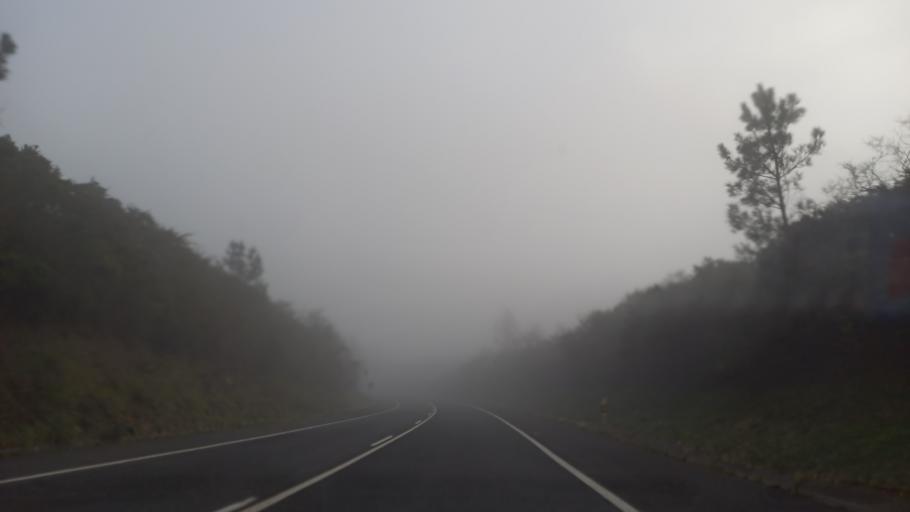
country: ES
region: Galicia
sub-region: Provincia da Coruna
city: As Pontes de Garcia Rodriguez
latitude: 43.4414
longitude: -7.9288
